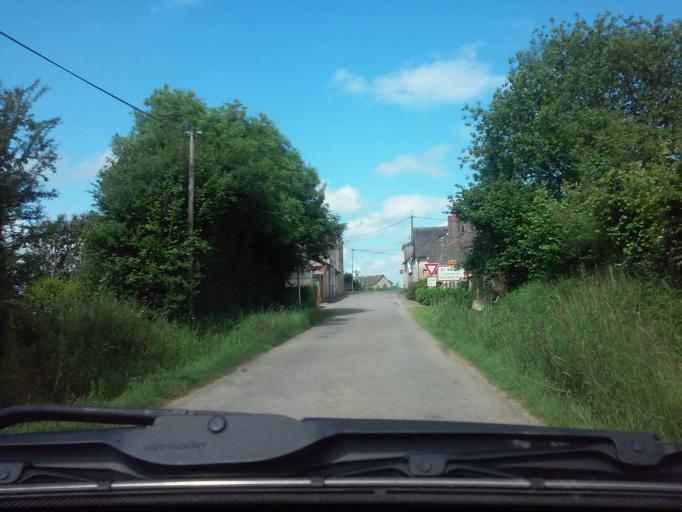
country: FR
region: Pays de la Loire
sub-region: Departement de la Mayenne
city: Quelaines-Saint-Gault
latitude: 47.8995
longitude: -0.7835
